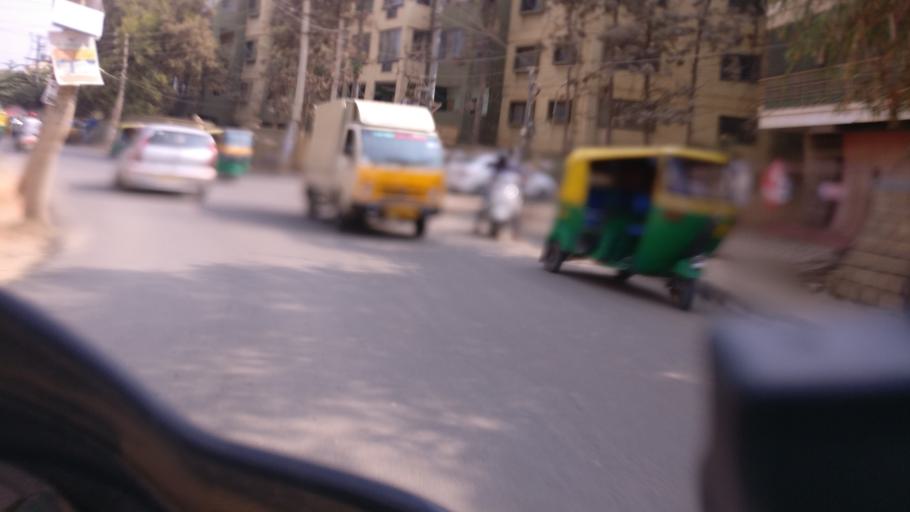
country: IN
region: Karnataka
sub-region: Bangalore Urban
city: Bangalore
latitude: 12.9101
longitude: 77.6765
